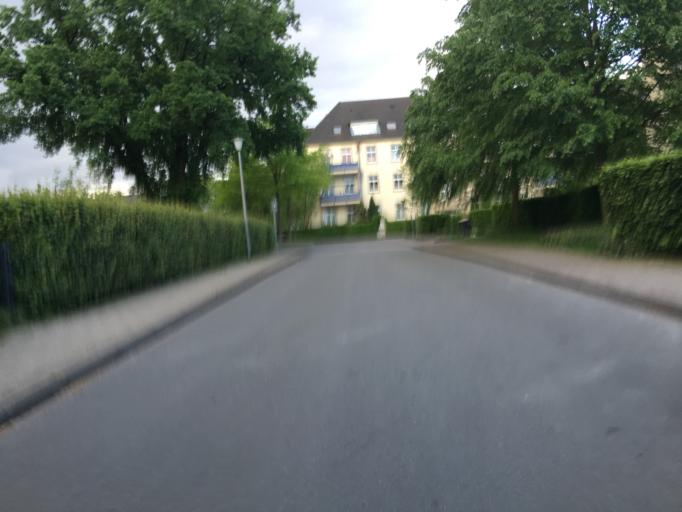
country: DE
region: North Rhine-Westphalia
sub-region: Regierungsbezirk Munster
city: Muenster
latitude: 51.9874
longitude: 7.6510
